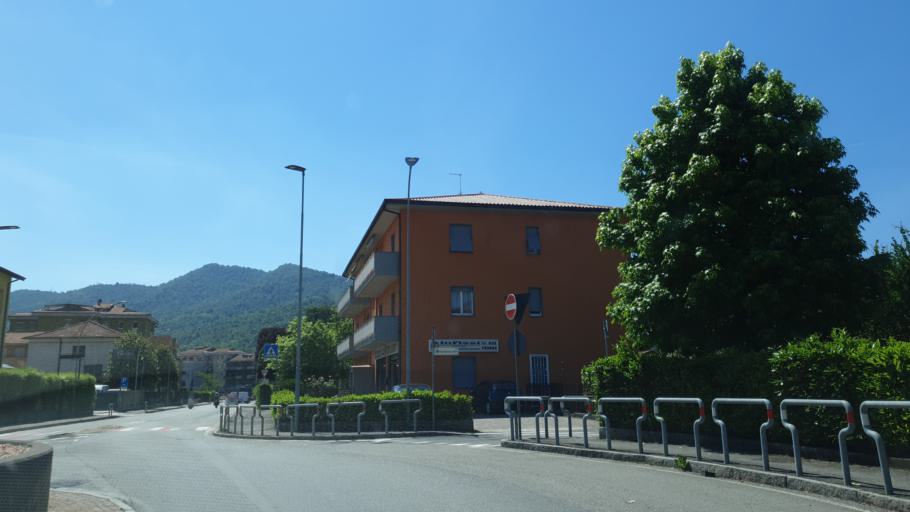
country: IT
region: Lombardy
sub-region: Provincia di Bergamo
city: Cisano Bergamasco
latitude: 45.7428
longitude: 9.4694
